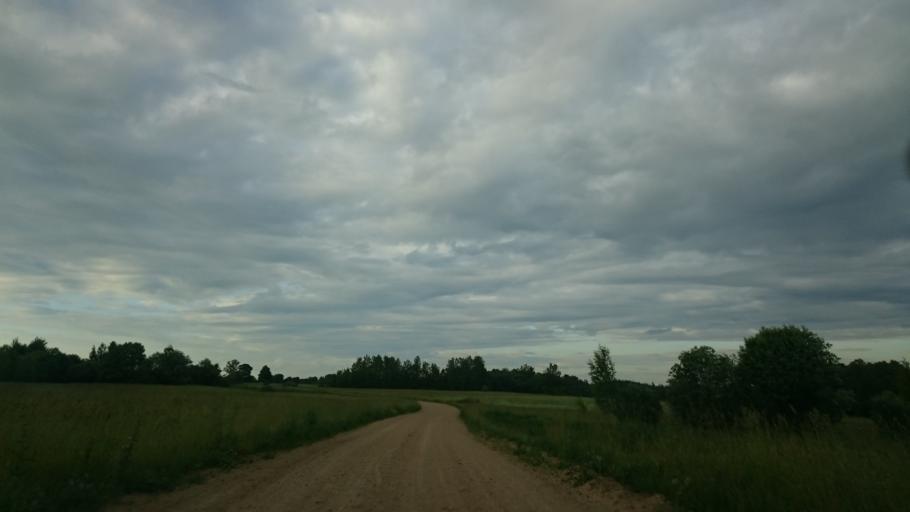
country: LV
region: Ludzas Rajons
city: Ludza
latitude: 56.5442
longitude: 27.6379
